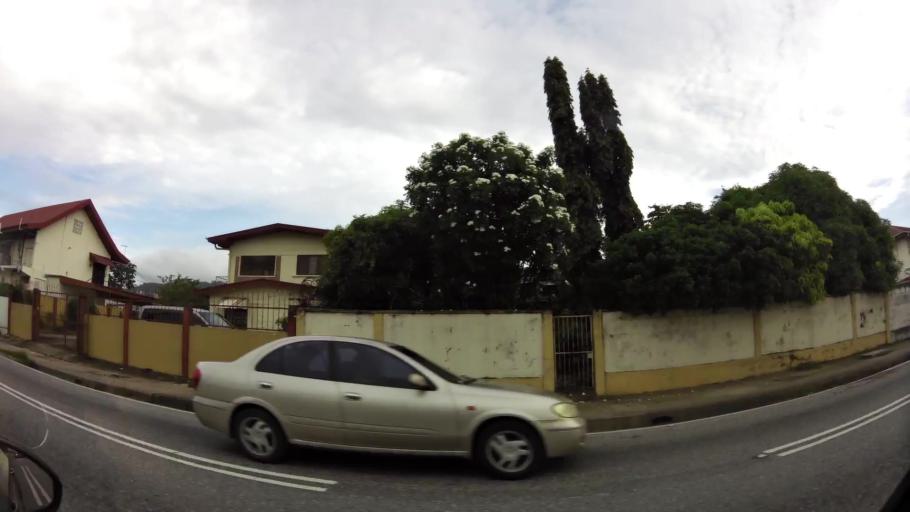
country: TT
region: Tunapuna/Piarco
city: Tunapuna
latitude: 10.6501
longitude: -61.4316
